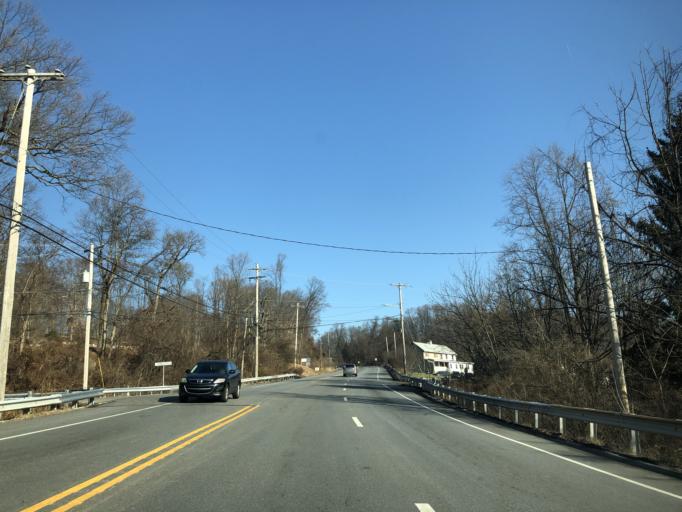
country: US
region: Pennsylvania
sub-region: Chester County
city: Downingtown
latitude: 40.0209
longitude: -75.6934
